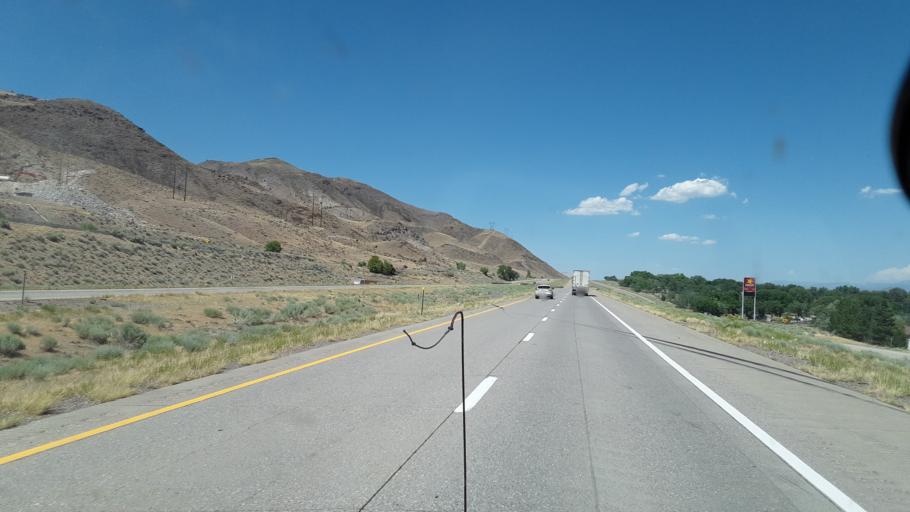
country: US
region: Utah
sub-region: Sevier County
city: Monroe
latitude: 38.6782
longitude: -112.1589
